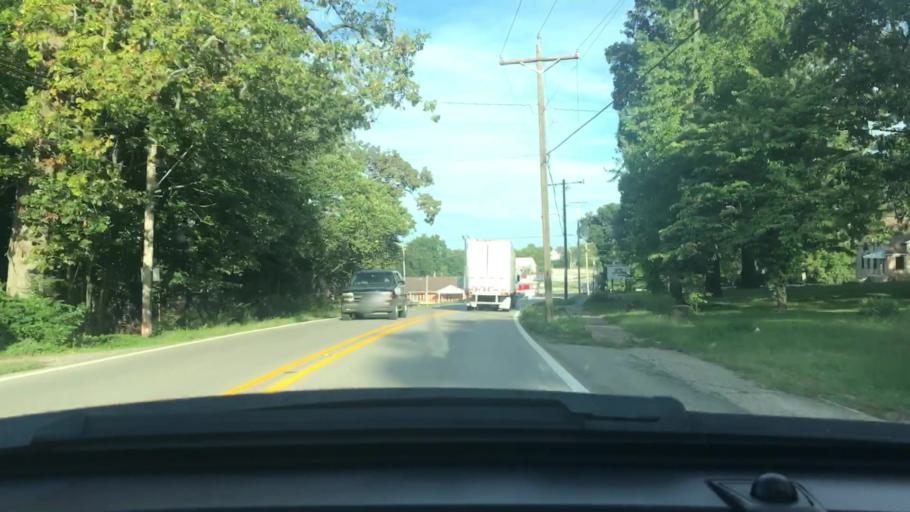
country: US
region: Arkansas
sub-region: Randolph County
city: Pocahontas
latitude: 36.2038
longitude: -91.1799
